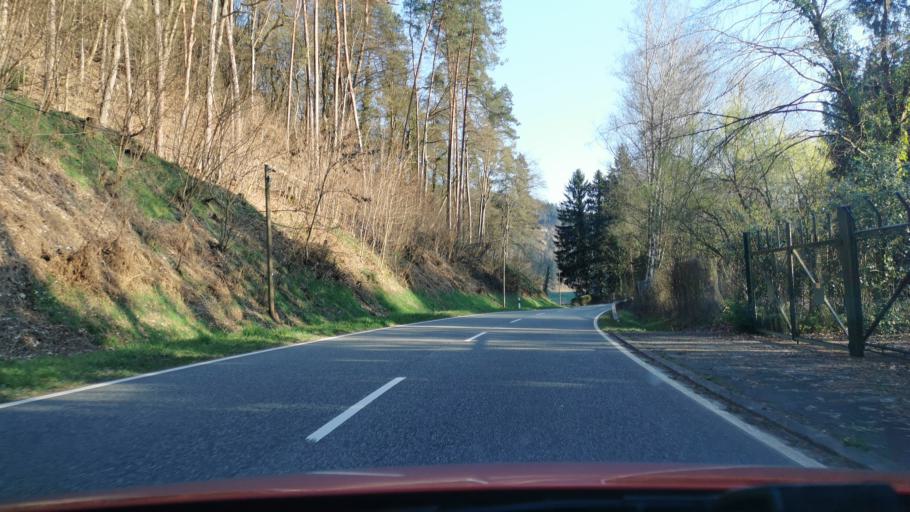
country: DE
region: Rheinland-Pfalz
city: Kordel
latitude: 49.8342
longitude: 6.6508
